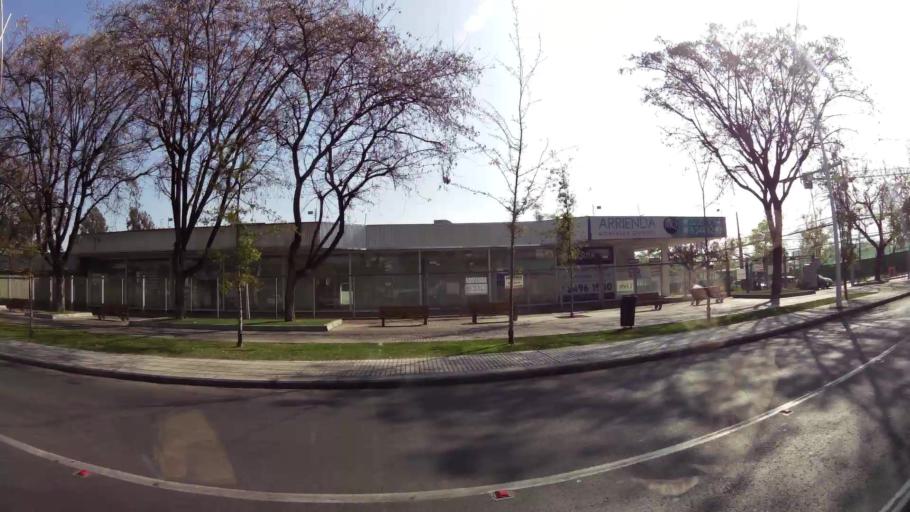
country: CL
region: Santiago Metropolitan
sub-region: Provincia de Santiago
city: Villa Presidente Frei, Nunoa, Santiago, Chile
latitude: -33.3873
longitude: -70.5648
